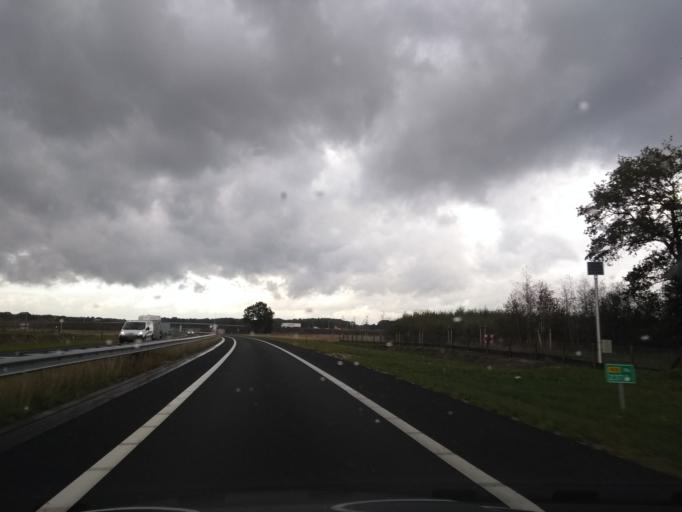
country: NL
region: Gelderland
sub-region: Berkelland
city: Eibergen
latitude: 52.0829
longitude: 6.6355
